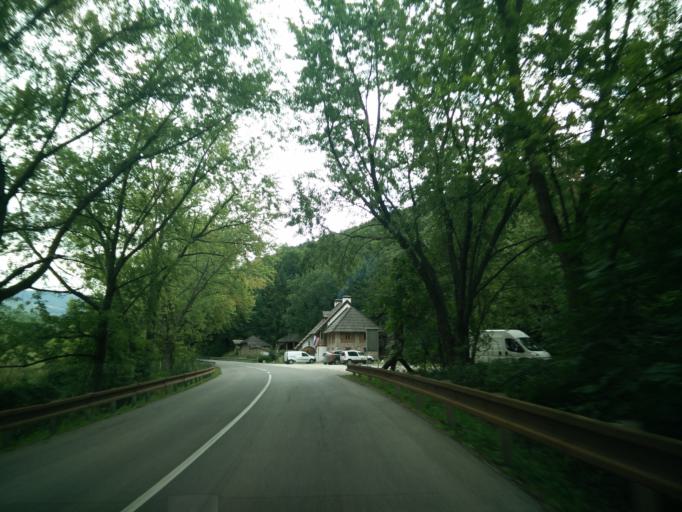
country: SK
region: Nitriansky
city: Novaky
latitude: 48.6004
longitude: 18.5022
